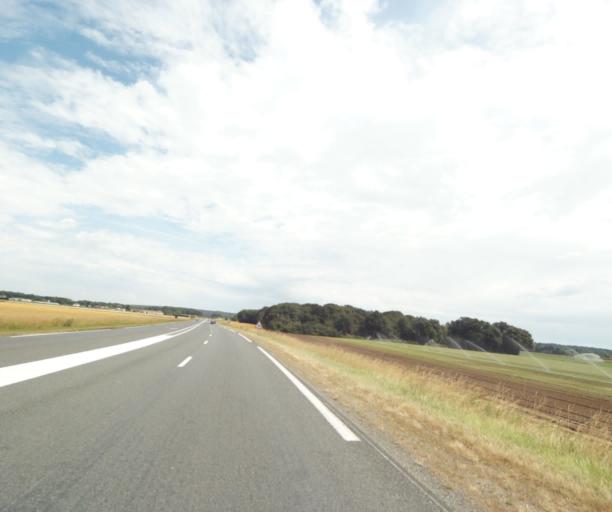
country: FR
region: Ile-de-France
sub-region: Departement de Seine-et-Marne
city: Barbizon
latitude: 48.4569
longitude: 2.5912
